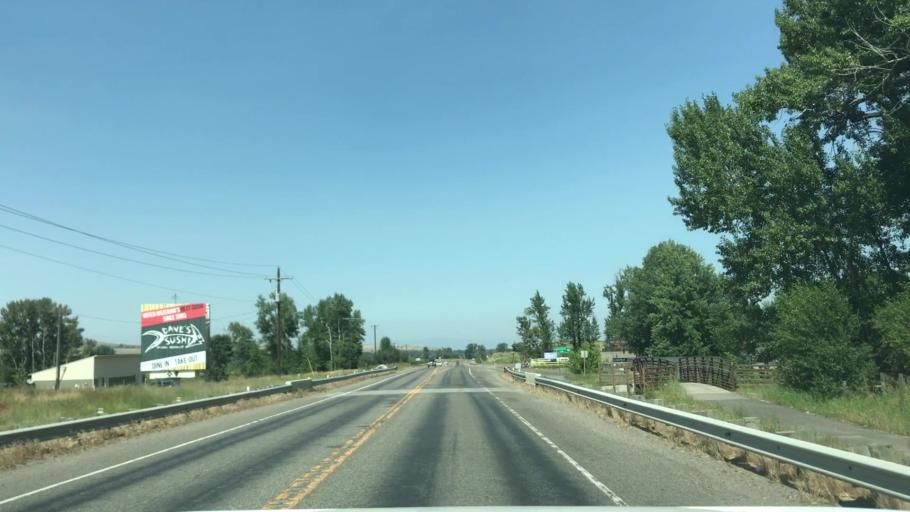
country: US
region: Montana
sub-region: Gallatin County
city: Four Corners
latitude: 45.6110
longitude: -111.1961
